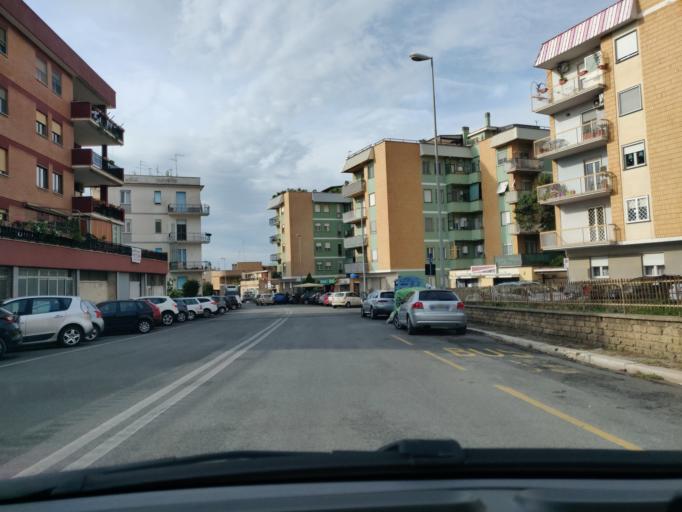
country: IT
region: Latium
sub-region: Citta metropolitana di Roma Capitale
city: Civitavecchia
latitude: 42.0969
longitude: 11.8046
